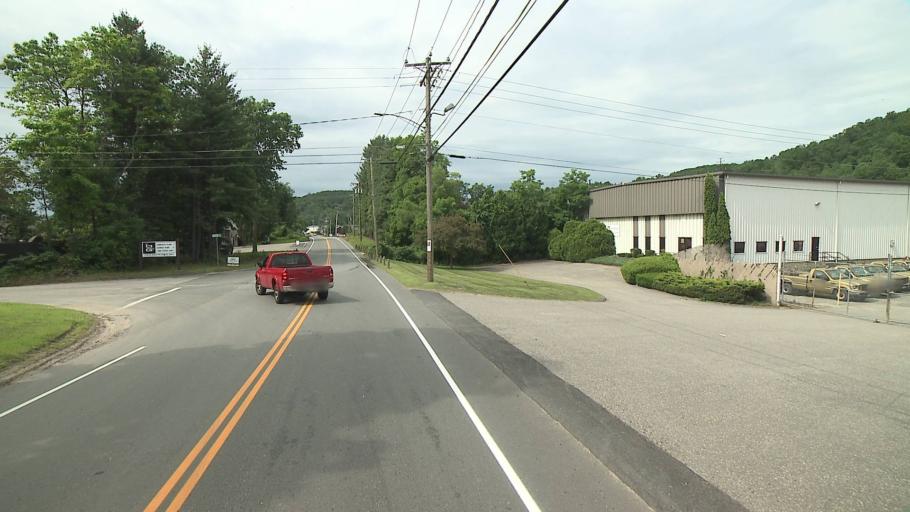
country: US
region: Connecticut
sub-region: Litchfield County
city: Torrington
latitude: 41.7776
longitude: -73.1194
